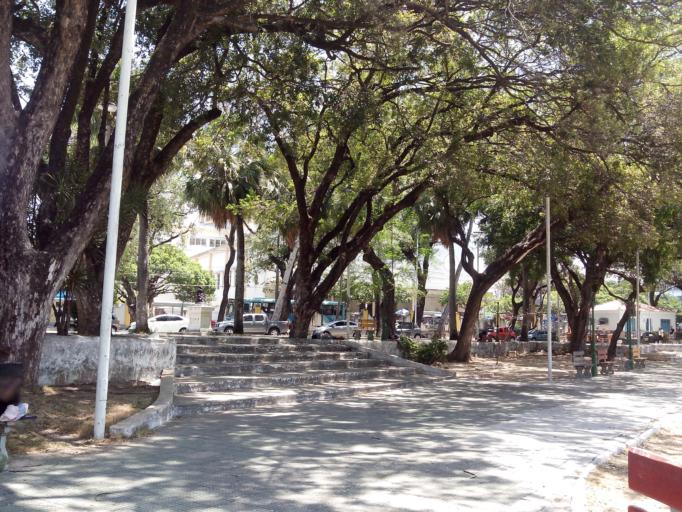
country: BR
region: Ceara
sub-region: Fortaleza
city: Fortaleza
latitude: -3.7318
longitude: -38.5255
